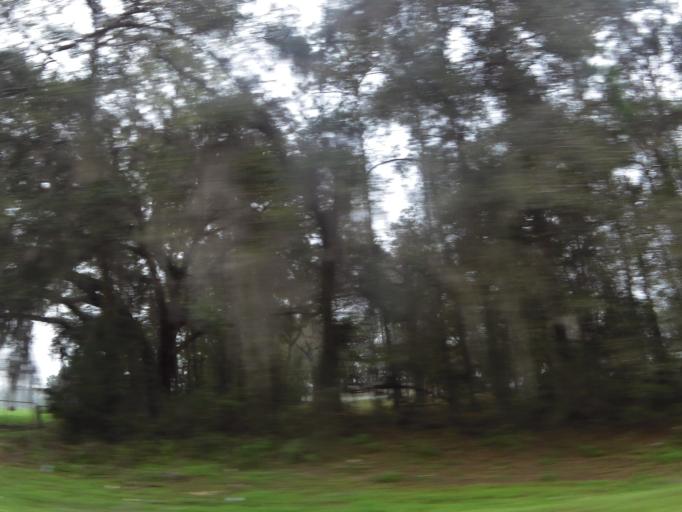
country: US
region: Florida
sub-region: Alachua County
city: Alachua
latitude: 29.8903
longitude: -82.4507
